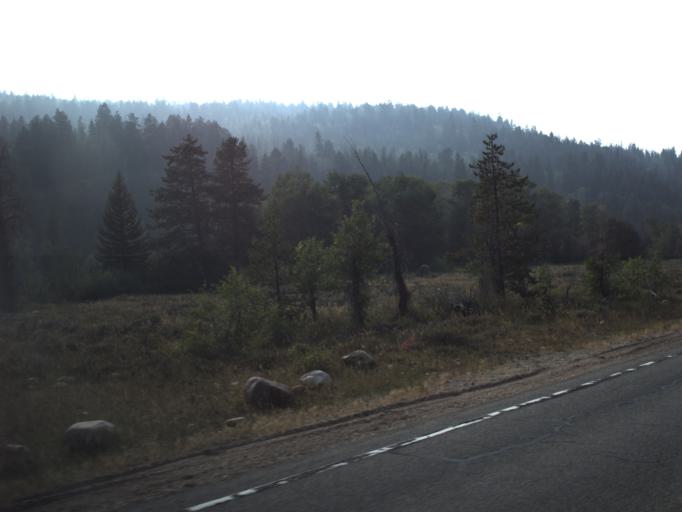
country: US
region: Utah
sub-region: Summit County
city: Francis
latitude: 40.6110
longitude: -111.1246
